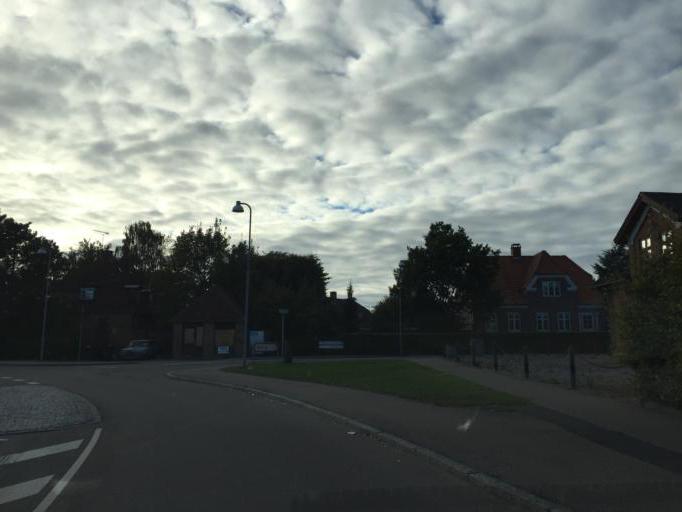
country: DK
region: Zealand
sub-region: Odsherred Kommune
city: Asnaes
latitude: 55.8129
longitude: 11.4989
